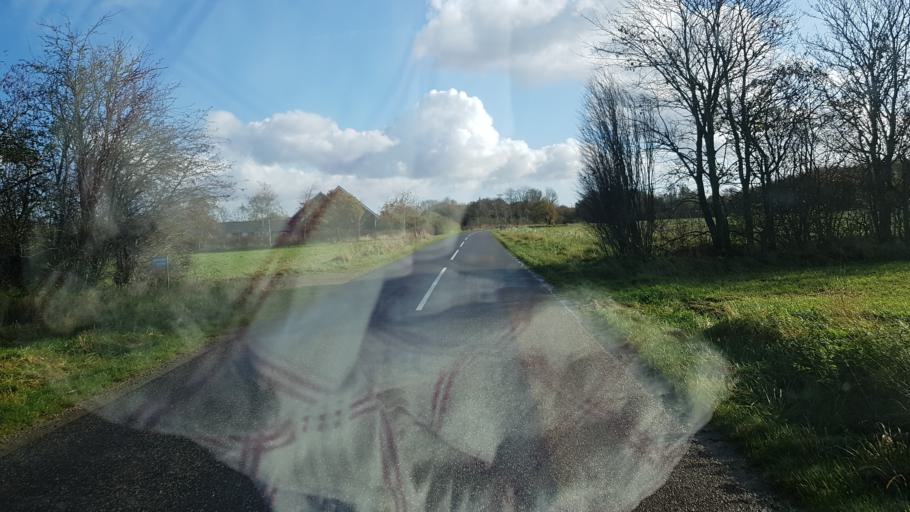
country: DK
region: South Denmark
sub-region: Varde Kommune
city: Olgod
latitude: 55.6914
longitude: 8.6545
